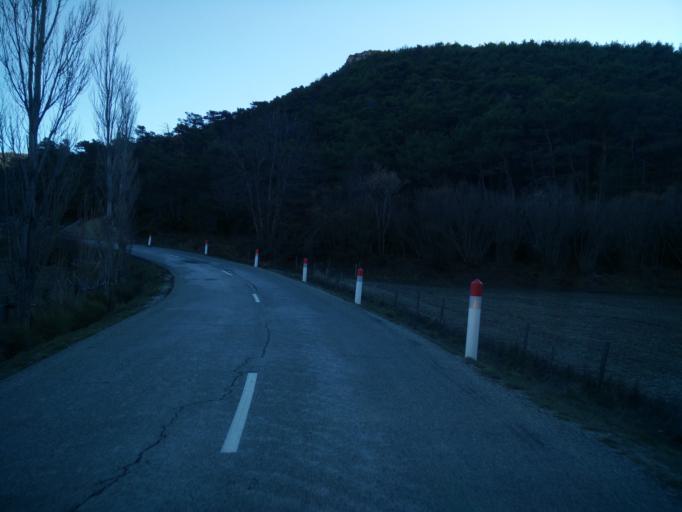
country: FR
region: Provence-Alpes-Cote d'Azur
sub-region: Departement des Alpes-de-Haute-Provence
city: Castellane
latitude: 43.7917
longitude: 6.3776
